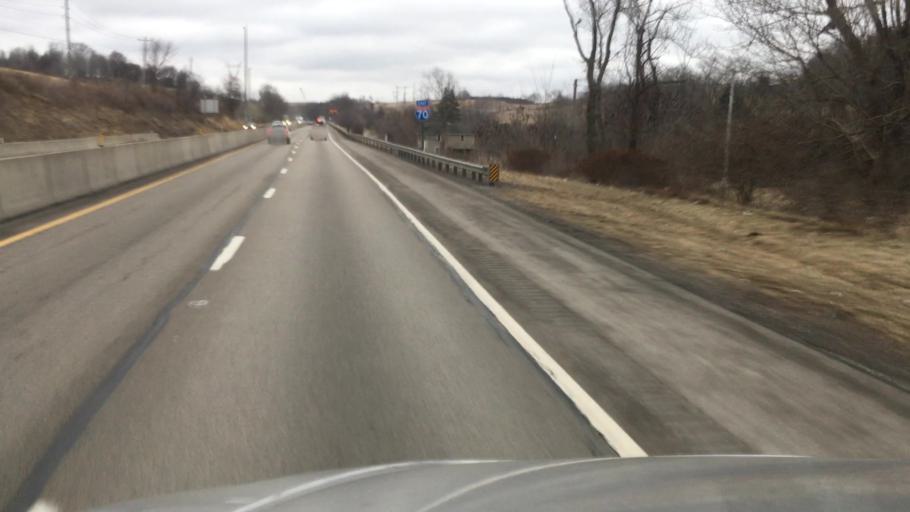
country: US
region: Pennsylvania
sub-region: Westmoreland County
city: West Newton
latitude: 40.1715
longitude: -79.7243
